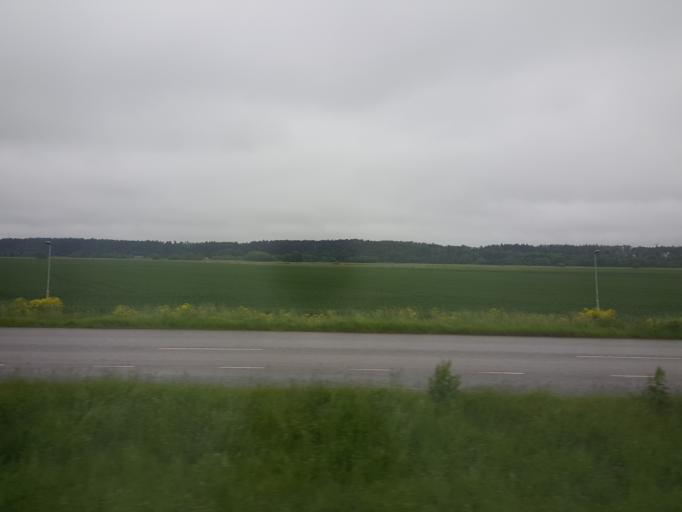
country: SE
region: Uppsala
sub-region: Uppsala Kommun
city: Saevja
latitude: 59.8397
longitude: 17.6825
